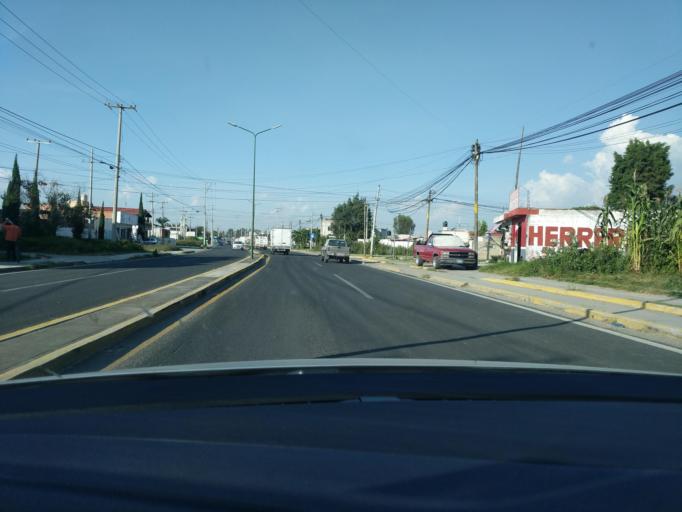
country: MX
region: Puebla
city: San Andres Cholula
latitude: 19.0370
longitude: -98.3161
